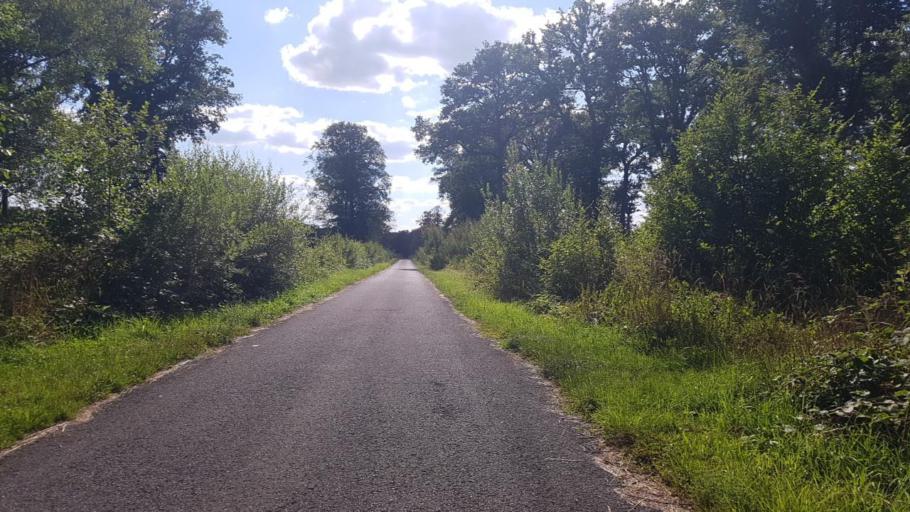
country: FR
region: Picardie
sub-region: Departement de l'Oise
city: Ver-sur-Launette
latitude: 49.1143
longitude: 2.6721
